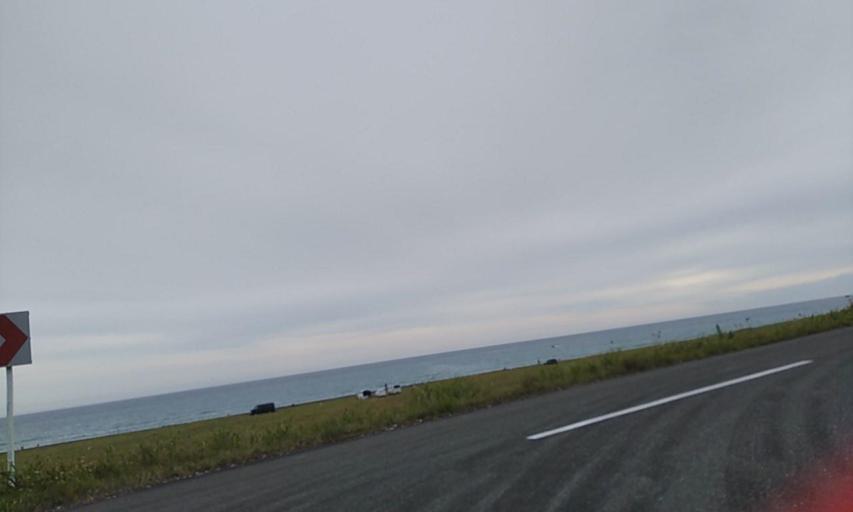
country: JP
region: Hokkaido
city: Makubetsu
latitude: 45.2690
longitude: 142.2381
